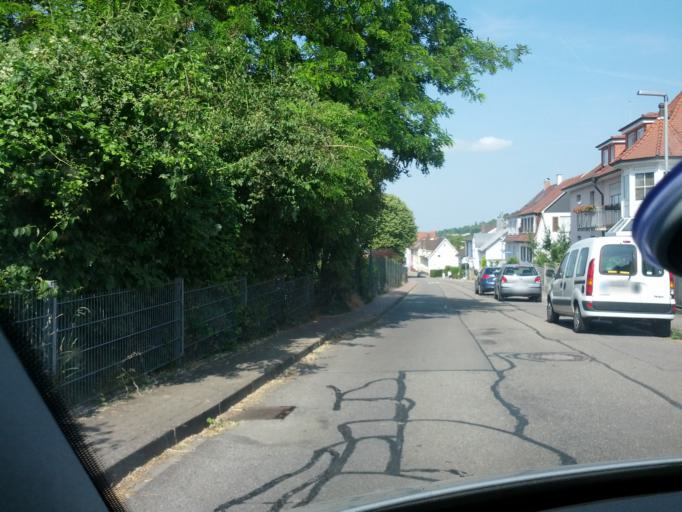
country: DE
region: Baden-Wuerttemberg
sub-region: Karlsruhe Region
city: Joehlingen
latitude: 49.0052
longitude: 8.5356
